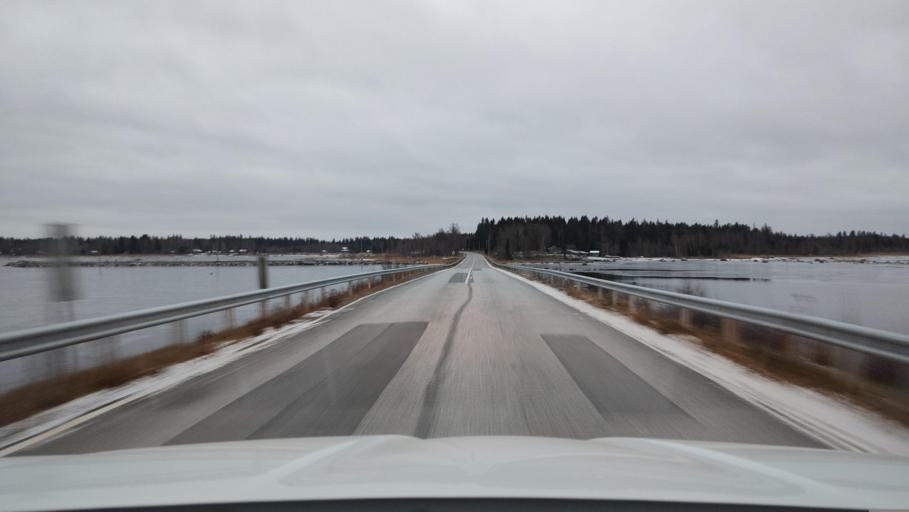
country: FI
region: Ostrobothnia
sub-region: Vaasa
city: Replot
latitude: 63.2738
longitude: 21.3438
